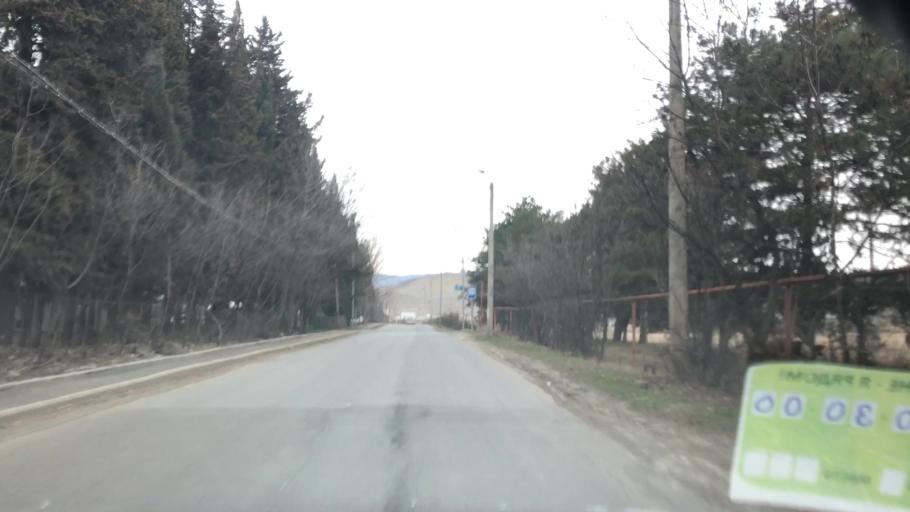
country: GE
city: Didi Lilo
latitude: 41.7022
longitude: 44.9286
